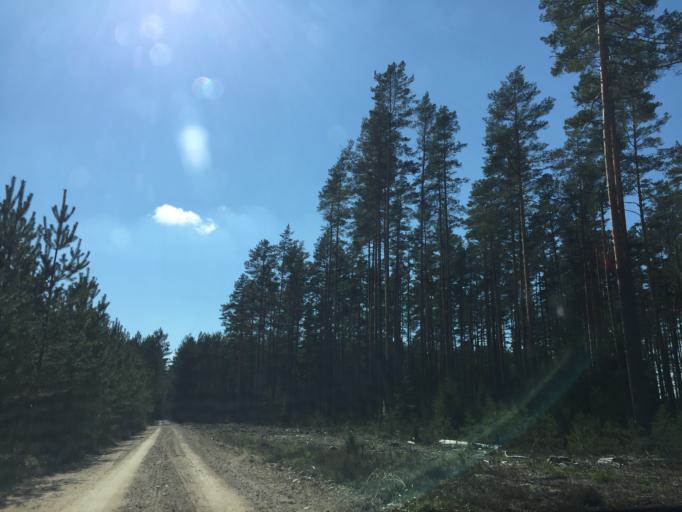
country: LV
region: Strenci
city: Strenci
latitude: 57.5944
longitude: 25.7001
